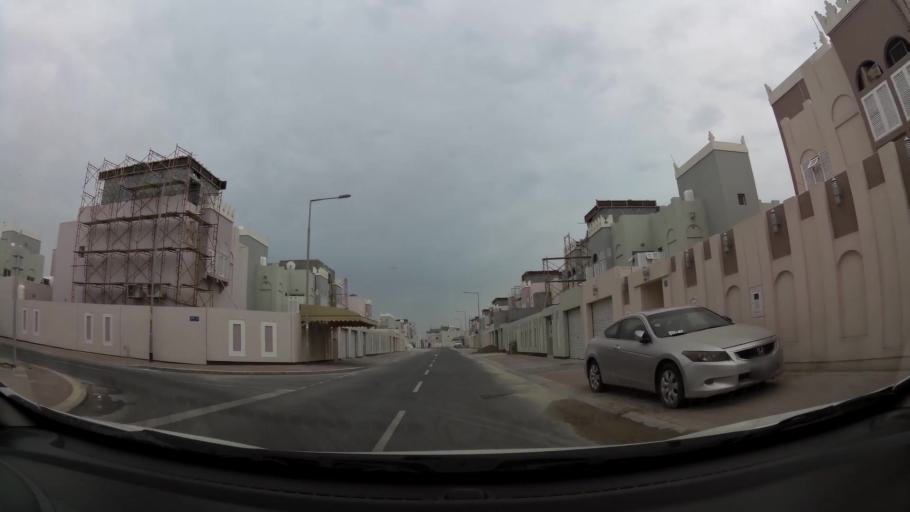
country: BH
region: Northern
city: Madinat `Isa
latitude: 26.1666
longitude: 50.5412
